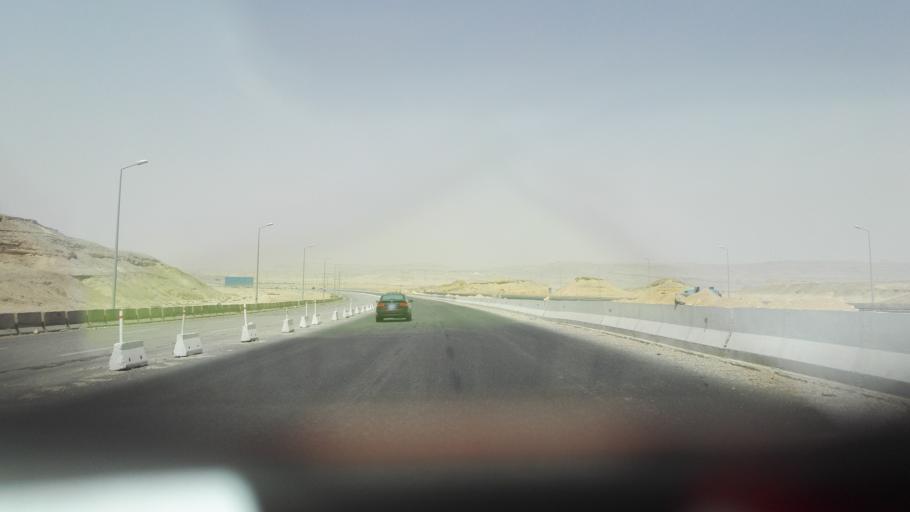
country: EG
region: As Suways
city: Ain Sukhna
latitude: 29.7546
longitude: 32.0234
